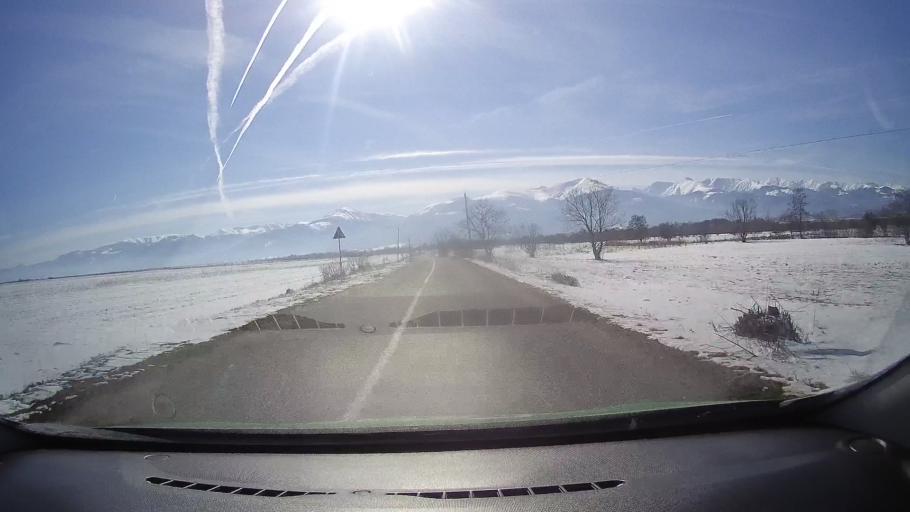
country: RO
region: Brasov
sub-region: Comuna Sambata de Sus
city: Sambata de Sus
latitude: 45.7451
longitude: 24.8430
